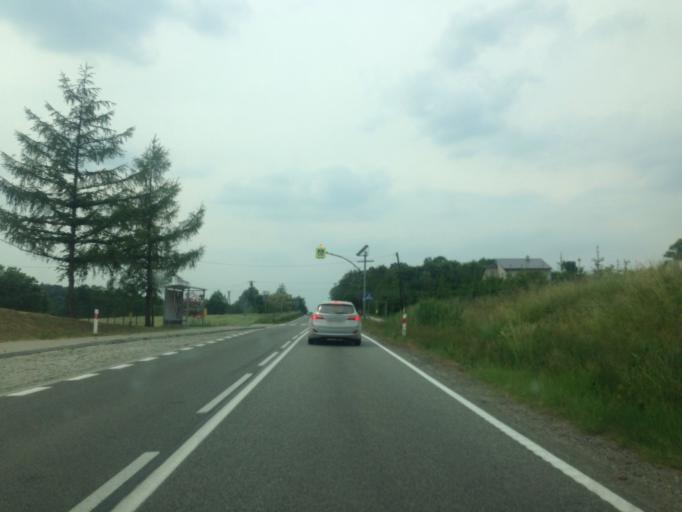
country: PL
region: Kujawsko-Pomorskie
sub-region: Powiat grudziadzki
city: Rogozno
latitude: 53.5006
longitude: 18.8795
